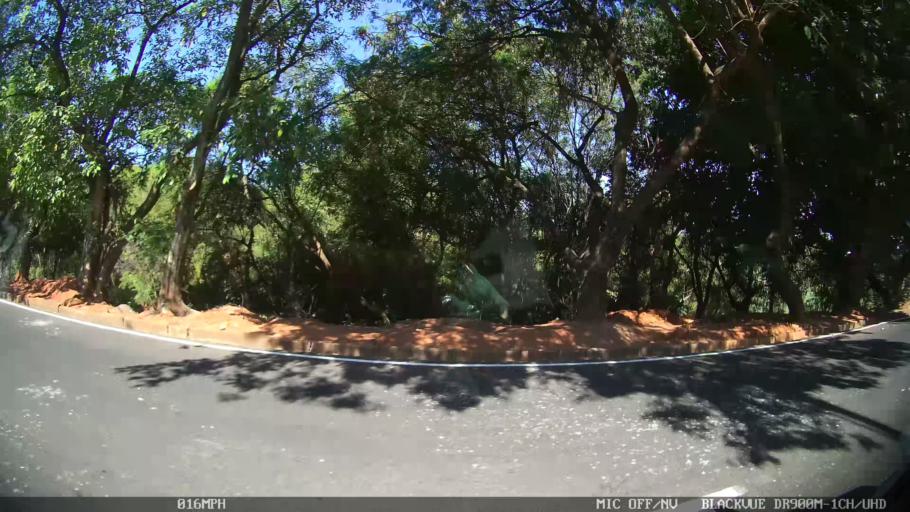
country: BR
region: Sao Paulo
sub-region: Sao Jose Do Rio Preto
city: Sao Jose do Rio Preto
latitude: -20.7730
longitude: -49.4077
